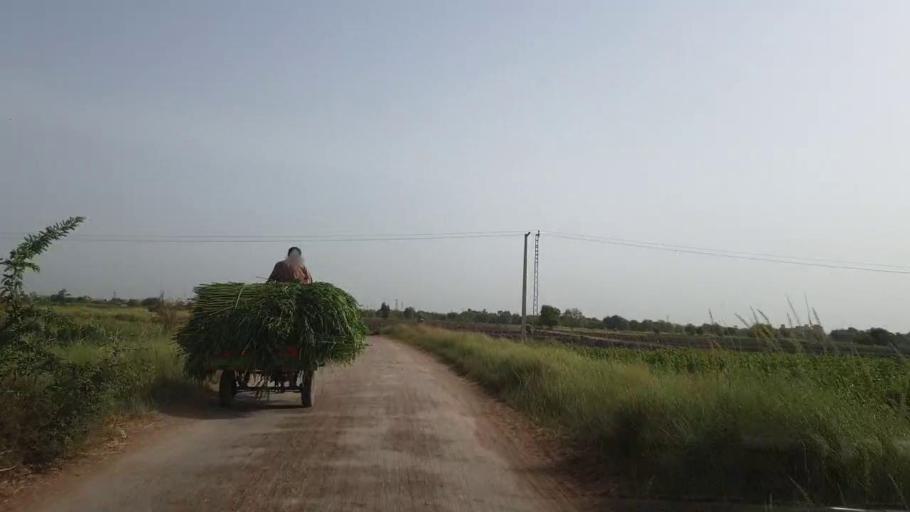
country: PK
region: Sindh
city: Nawabshah
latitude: 26.2246
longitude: 68.4056
